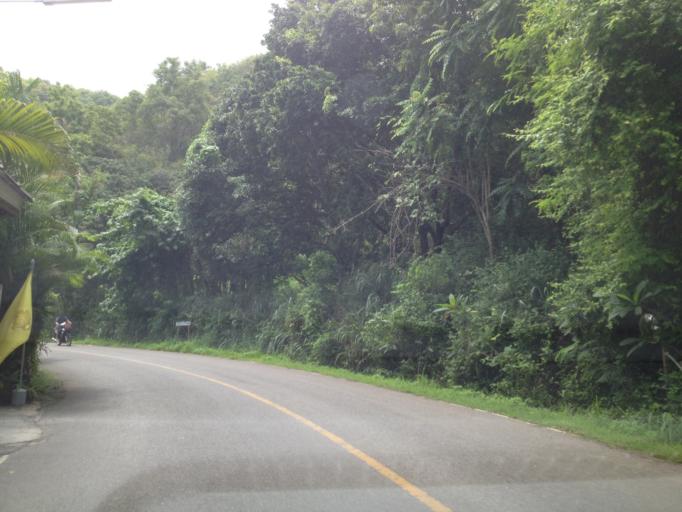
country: TH
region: Chiang Mai
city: Chiang Mai
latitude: 18.7622
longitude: 98.9201
